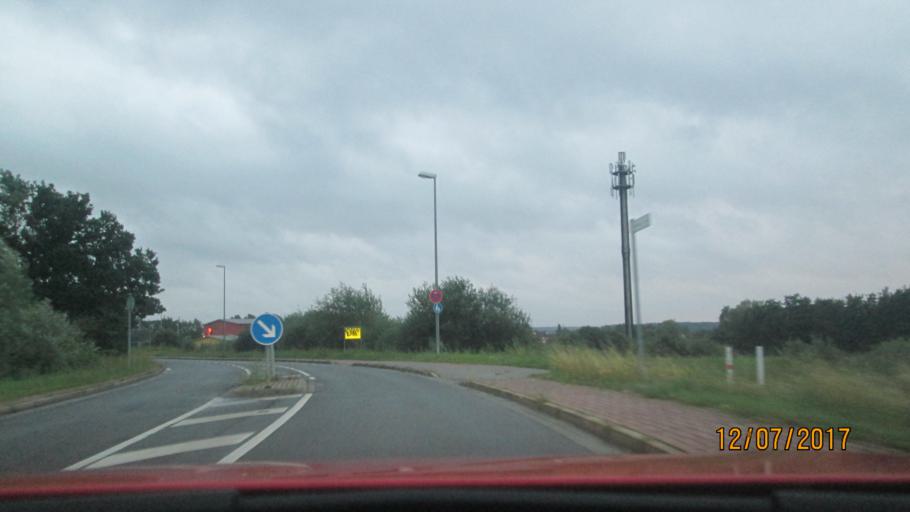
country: DE
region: Lower Saxony
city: Weyhausen
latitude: 52.4003
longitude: 10.7155
